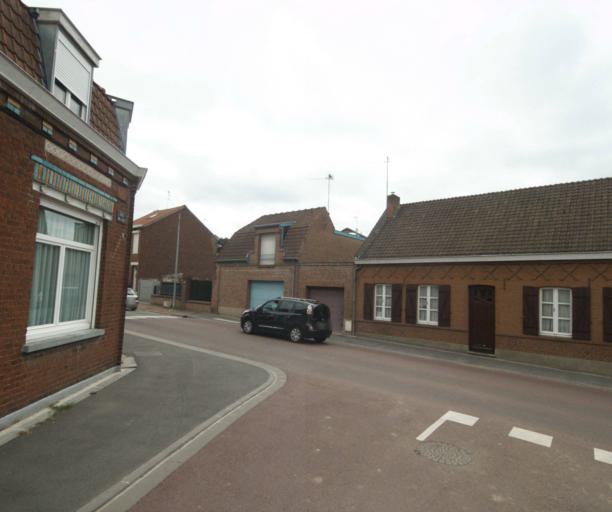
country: FR
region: Nord-Pas-de-Calais
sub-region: Departement du Nord
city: Toufflers
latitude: 50.6624
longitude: 3.2293
